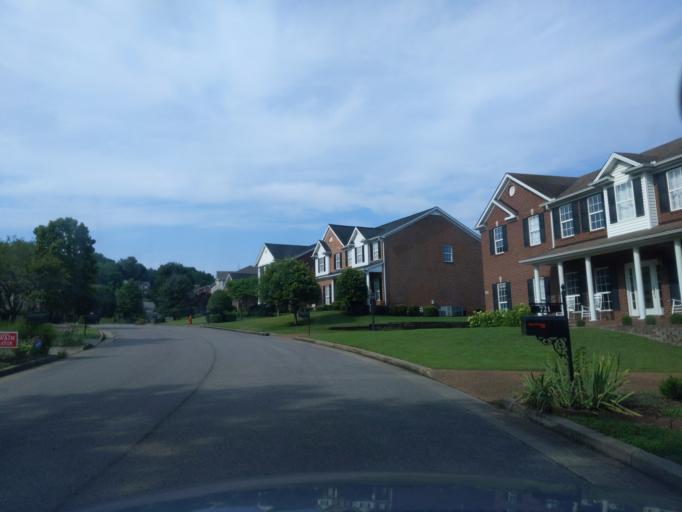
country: US
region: Tennessee
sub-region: Williamson County
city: Brentwood Estates
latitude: 36.0246
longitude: -86.7500
